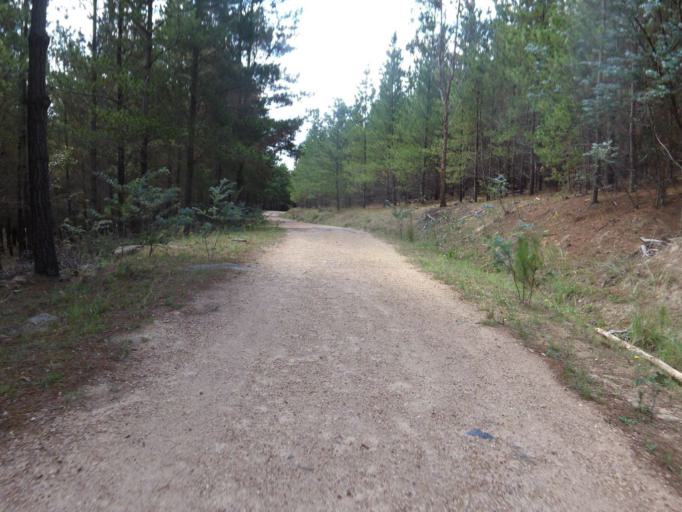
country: AU
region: Australian Capital Territory
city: Macarthur
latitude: -35.3807
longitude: 149.1209
